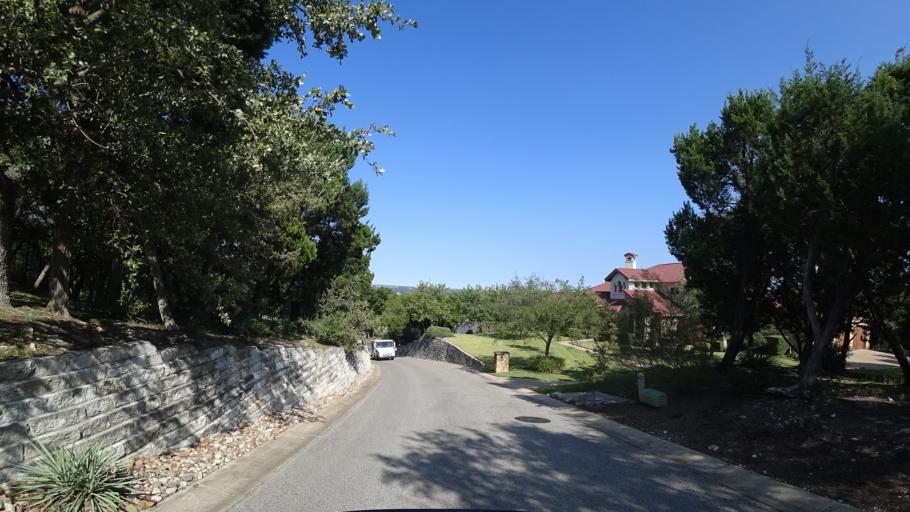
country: US
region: Texas
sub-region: Travis County
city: West Lake Hills
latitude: 30.2879
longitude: -97.8064
